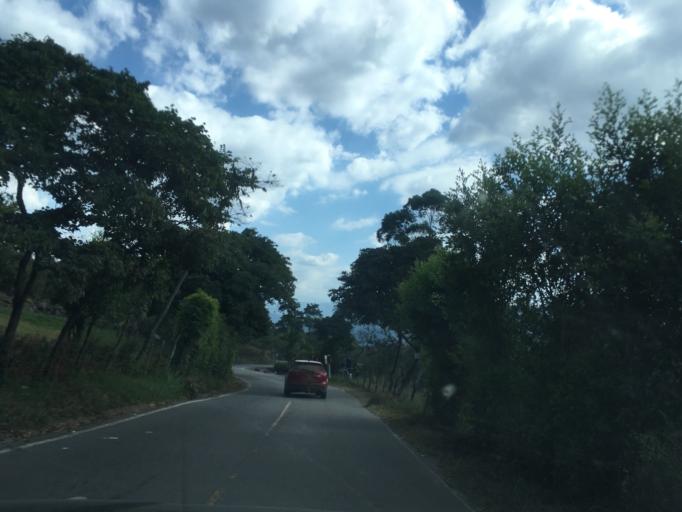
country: CO
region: Santander
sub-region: San Gil
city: San Gil
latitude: 6.5829
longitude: -73.1572
